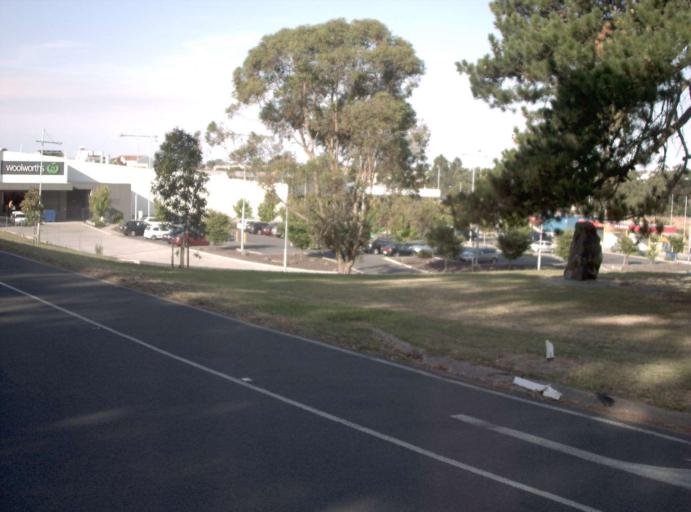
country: AU
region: Victoria
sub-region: Latrobe
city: Morwell
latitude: -38.3151
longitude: 146.4193
